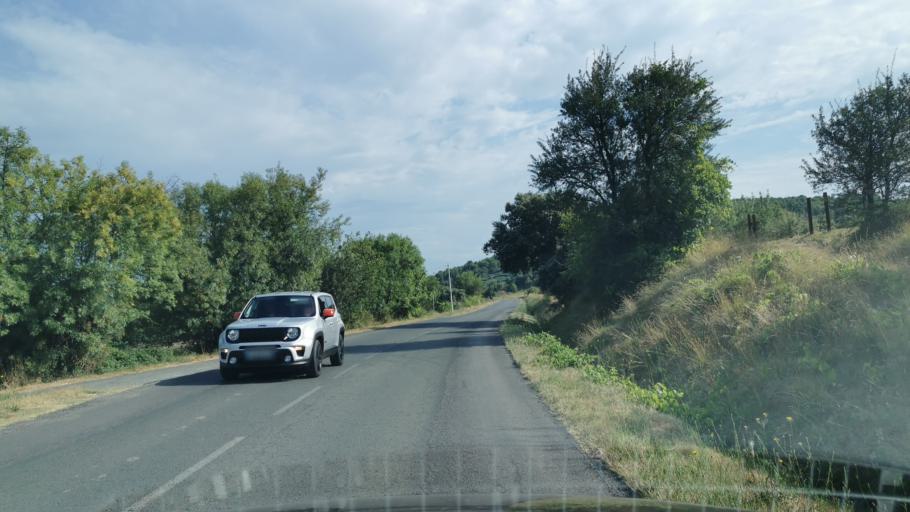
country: FR
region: Languedoc-Roussillon
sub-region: Departement de l'Aude
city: Bize-Minervois
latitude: 43.3032
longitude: 2.8700
